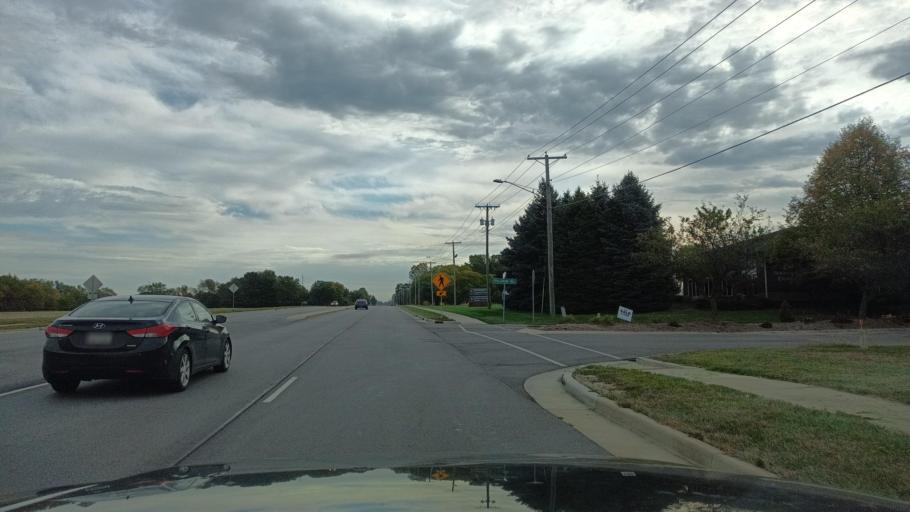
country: US
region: Indiana
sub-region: Delaware County
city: Yorktown
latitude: 40.1812
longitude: -85.4739
